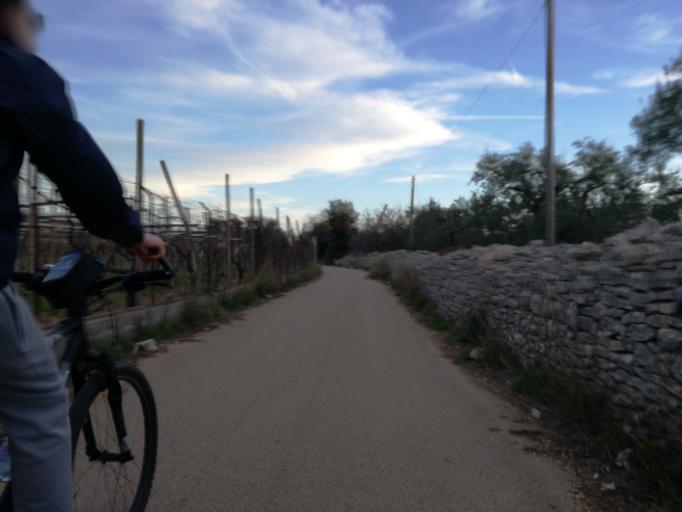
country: IT
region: Apulia
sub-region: Provincia di Bari
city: Adelfia
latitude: 41.0173
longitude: 16.8717
